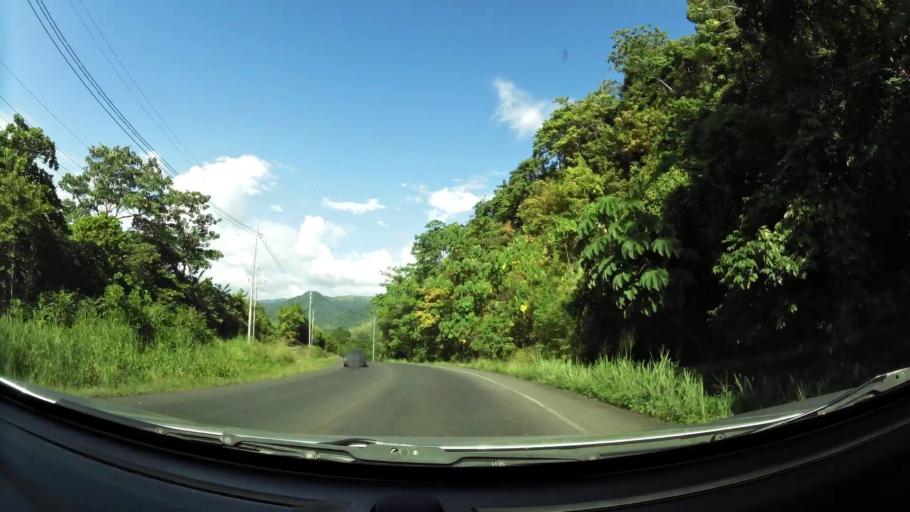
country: CR
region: Puntarenas
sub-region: Canton de Garabito
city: Jaco
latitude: 9.5948
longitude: -84.6210
